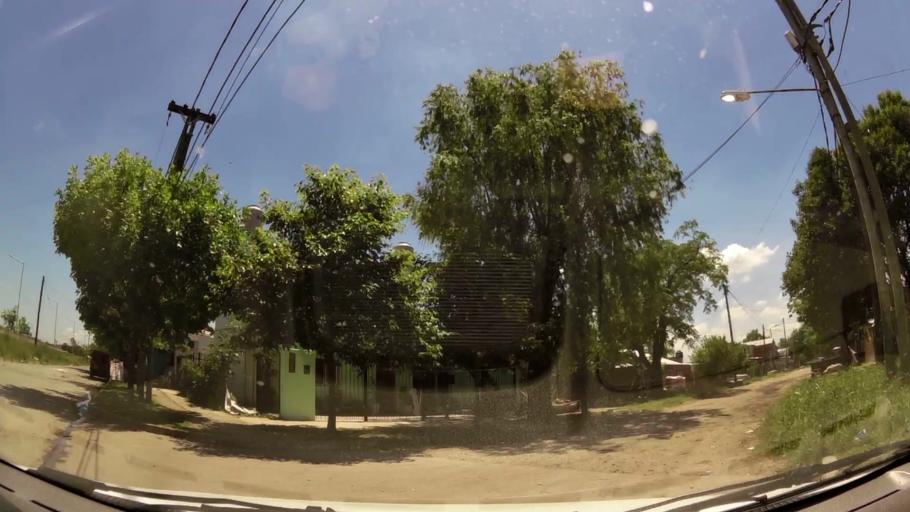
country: AR
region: Buenos Aires
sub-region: Partido de Merlo
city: Merlo
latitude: -34.6509
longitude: -58.7042
